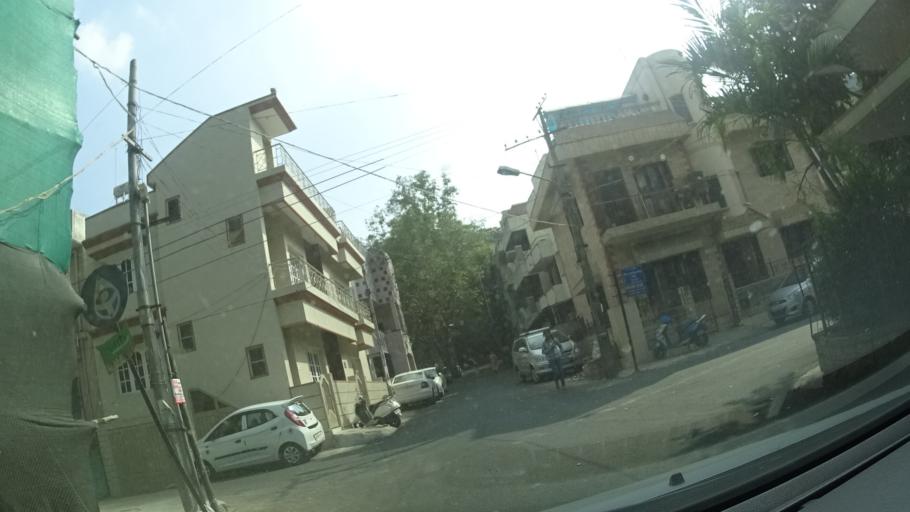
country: IN
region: Karnataka
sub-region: Bangalore Urban
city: Bangalore
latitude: 12.9459
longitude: 77.5633
